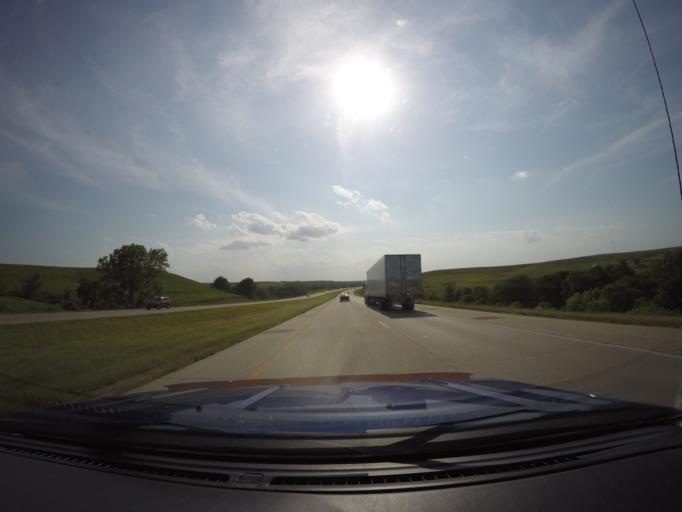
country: US
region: Kansas
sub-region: Wabaunsee County
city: Alma
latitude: 39.0646
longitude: -96.4393
